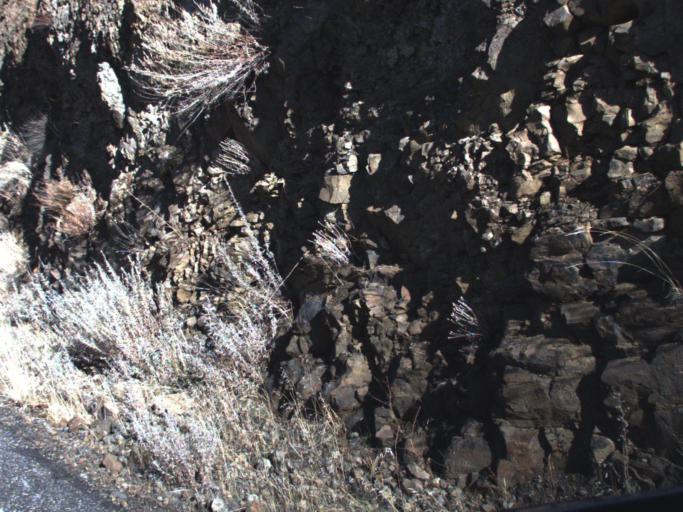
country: US
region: Washington
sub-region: Asotin County
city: Asotin
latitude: 46.0556
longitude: -117.2339
